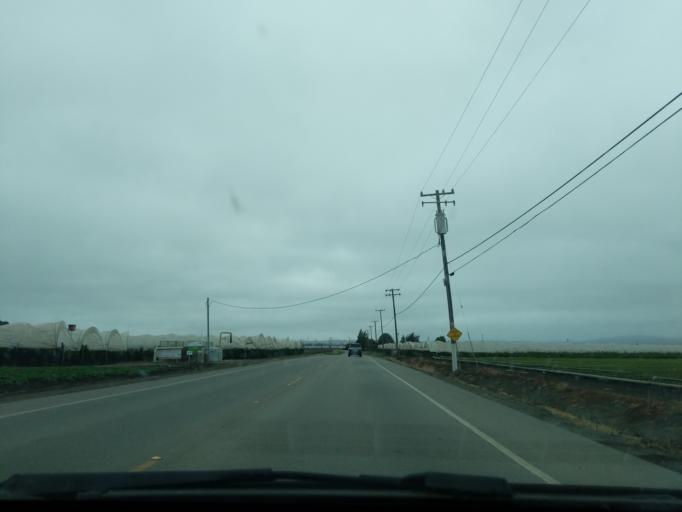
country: US
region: California
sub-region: Monterey County
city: Pajaro
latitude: 36.9028
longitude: -121.6991
